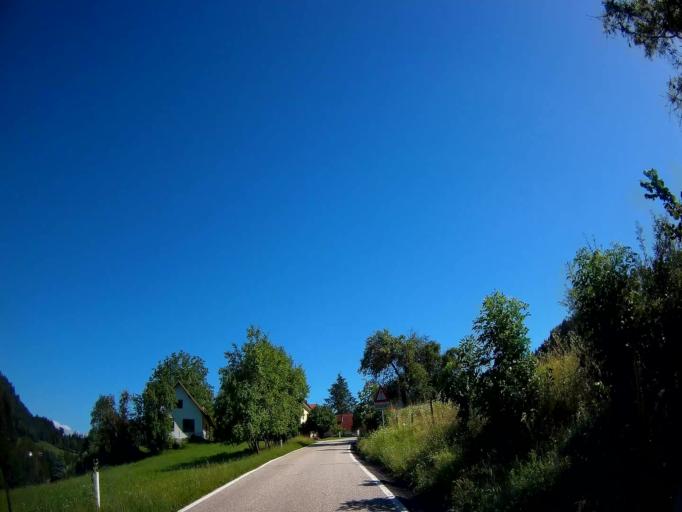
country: AT
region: Carinthia
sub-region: Politischer Bezirk Volkermarkt
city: Diex
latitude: 46.6907
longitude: 14.5779
